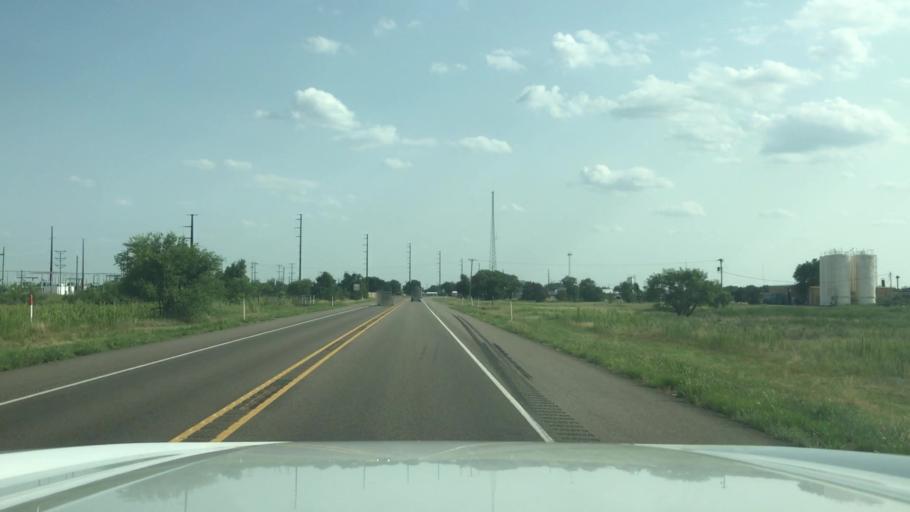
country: US
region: Texas
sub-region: Hartley County
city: Channing
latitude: 35.6923
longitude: -102.3283
